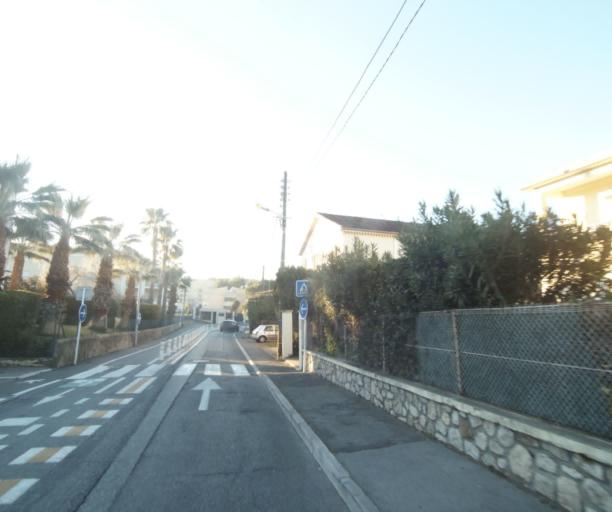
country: FR
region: Provence-Alpes-Cote d'Azur
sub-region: Departement des Alpes-Maritimes
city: Vallauris
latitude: 43.5754
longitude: 7.0872
